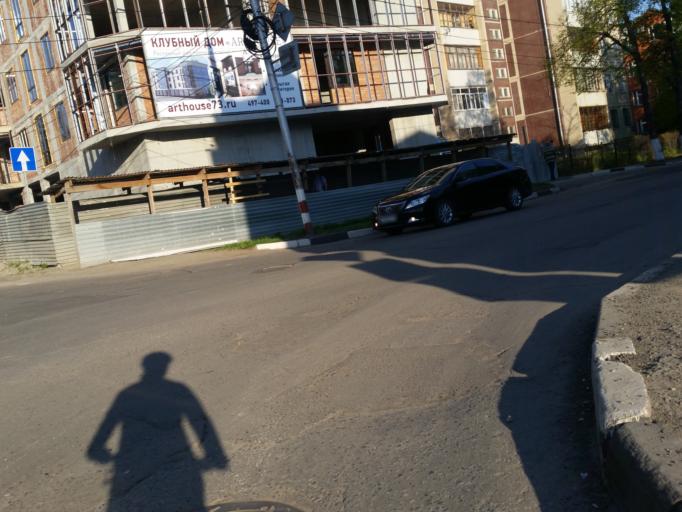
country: RU
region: Ulyanovsk
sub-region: Ulyanovskiy Rayon
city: Ulyanovsk
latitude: 54.3275
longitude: 48.3983
